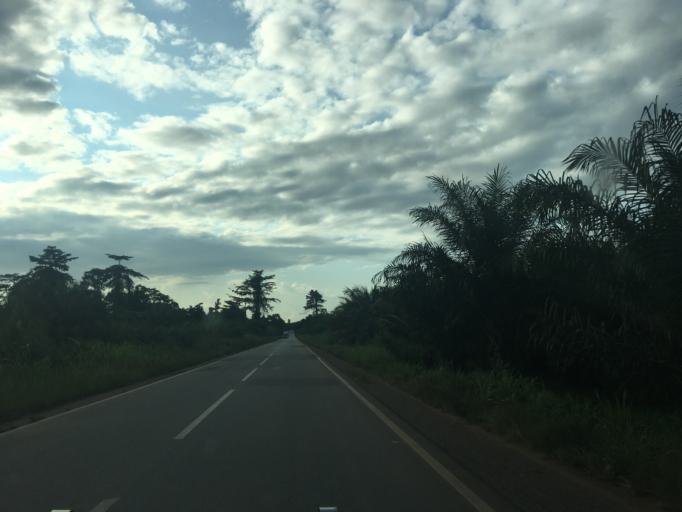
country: GH
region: Western
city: Bibiani
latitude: 6.3583
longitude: -2.2835
